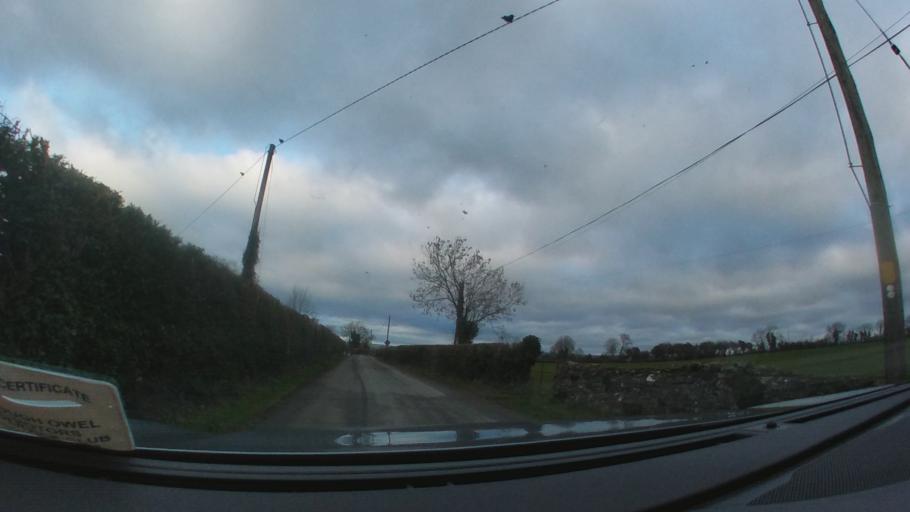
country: IE
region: Leinster
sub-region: Kilkenny
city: Thomastown
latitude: 52.5695
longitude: -7.1461
